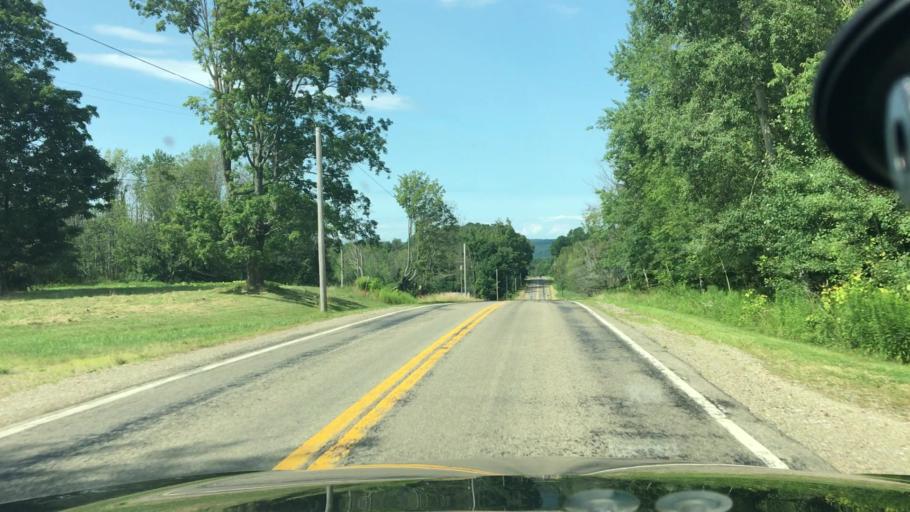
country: US
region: New York
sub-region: Chautauqua County
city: Lakewood
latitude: 42.2405
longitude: -79.3589
